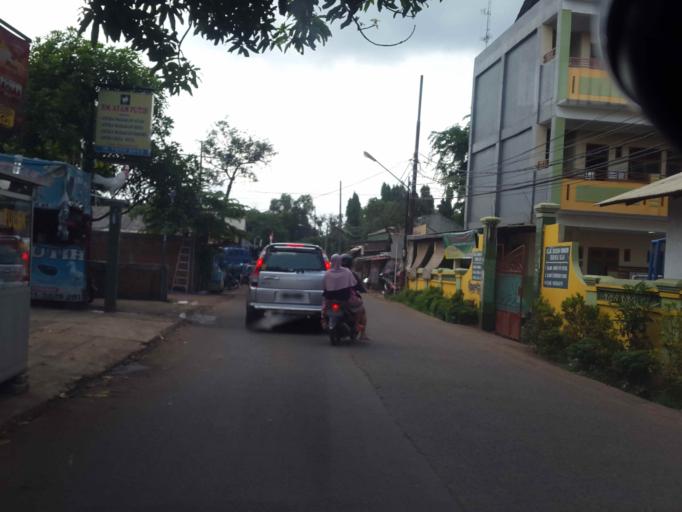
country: ID
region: West Java
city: Cileungsir
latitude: -6.3201
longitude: 106.9487
